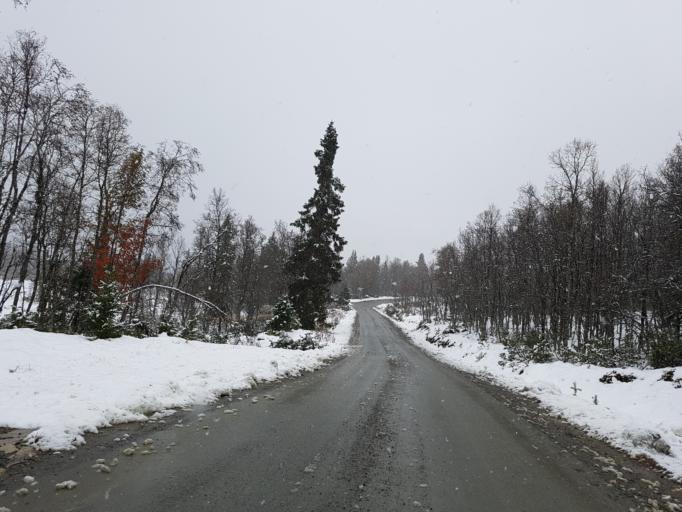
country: NO
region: Oppland
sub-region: Sel
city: Otta
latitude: 61.7908
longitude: 9.7190
